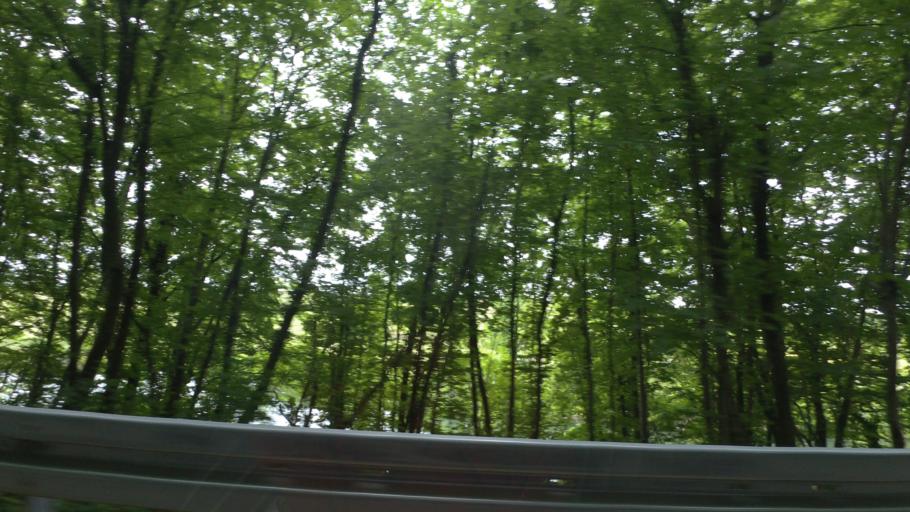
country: HR
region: Karlovacka
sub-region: Grad Karlovac
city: Karlovac
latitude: 45.4244
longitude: 15.5662
